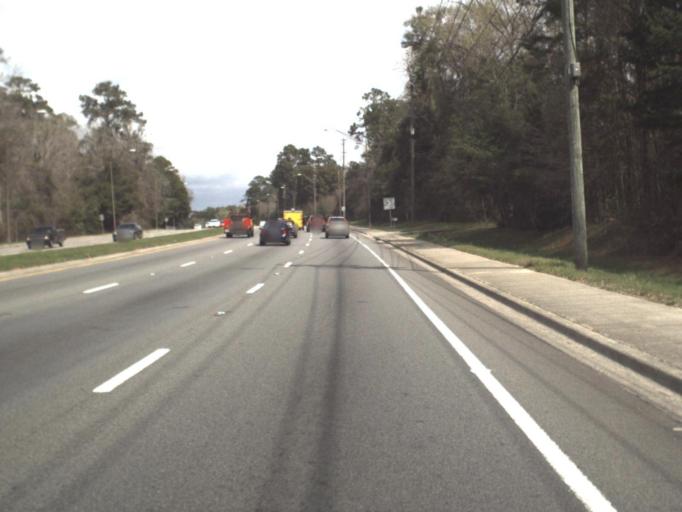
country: US
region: Florida
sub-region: Leon County
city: Tallahassee
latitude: 30.5140
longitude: -84.2429
